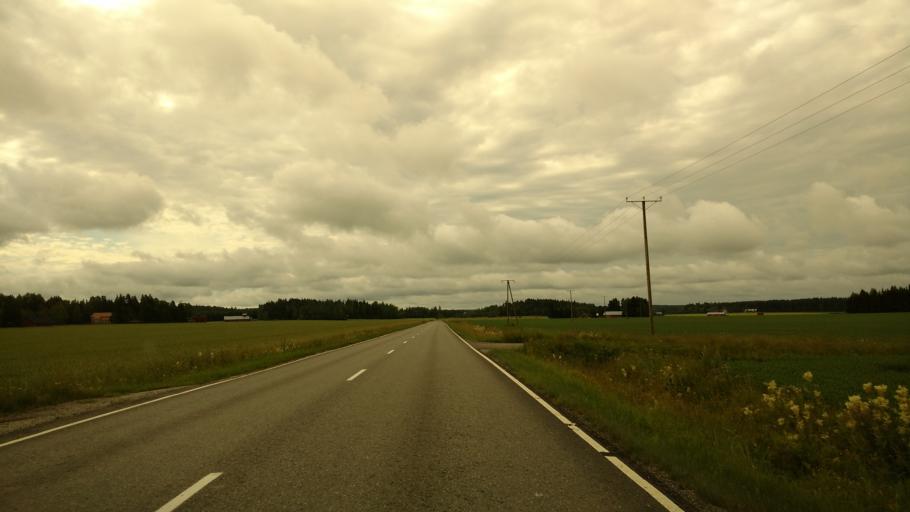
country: FI
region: Varsinais-Suomi
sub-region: Salo
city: Kuusjoki
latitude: 60.4934
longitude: 23.1653
